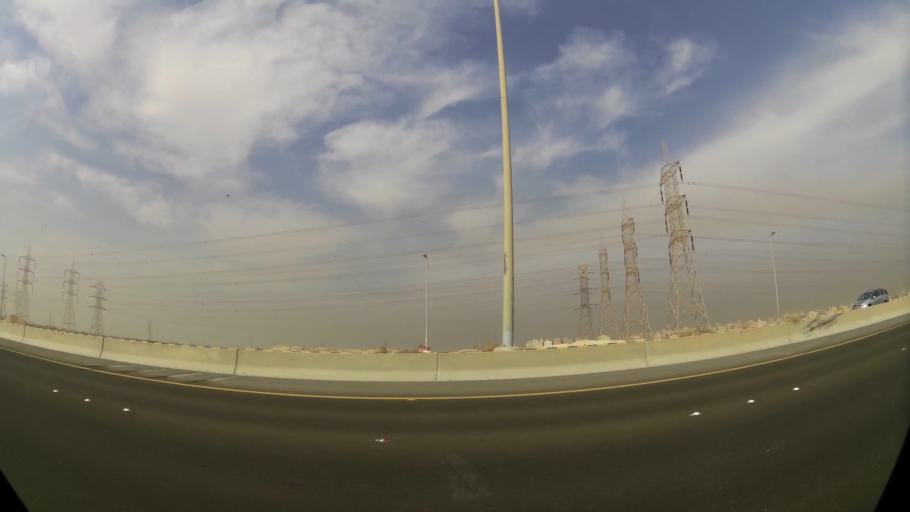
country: KW
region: Muhafazat al Jahra'
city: Al Jahra'
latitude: 29.3223
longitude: 47.7854
